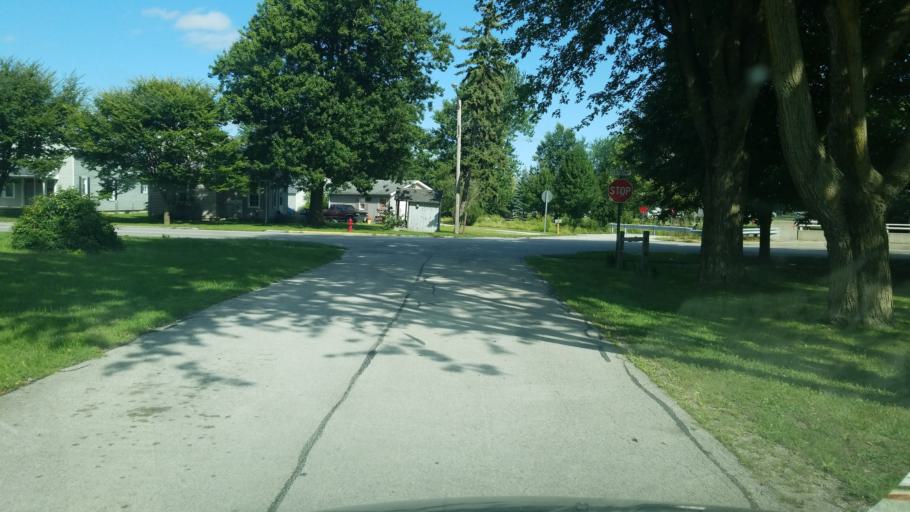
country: US
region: Ohio
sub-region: Seneca County
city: Fostoria
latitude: 41.1098
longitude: -83.5103
